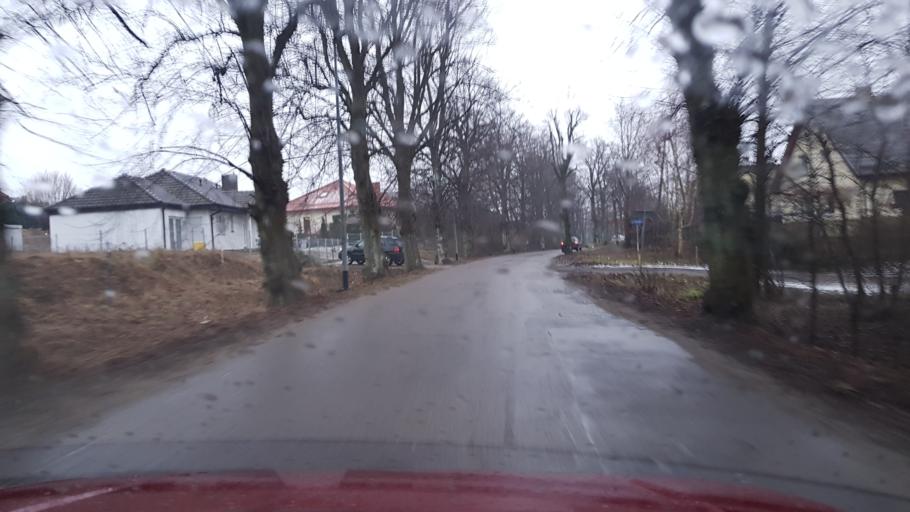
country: PL
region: West Pomeranian Voivodeship
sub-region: Powiat koszalinski
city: Sianow
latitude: 54.1839
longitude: 16.2446
